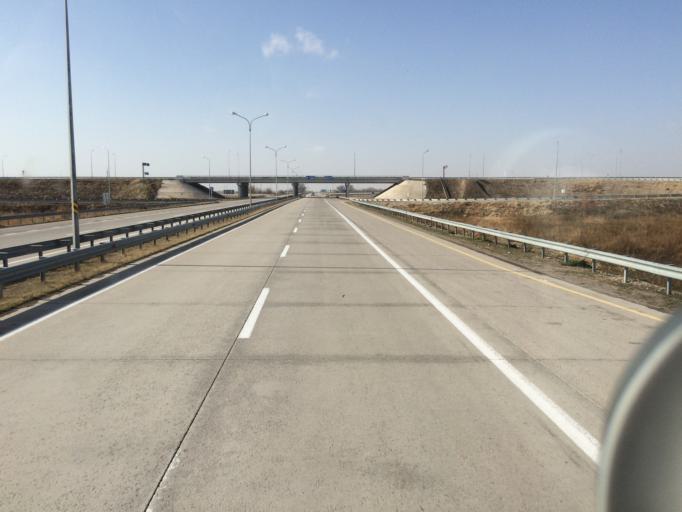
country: KZ
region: Zhambyl
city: Oytal
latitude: 42.9284
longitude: 73.2453
